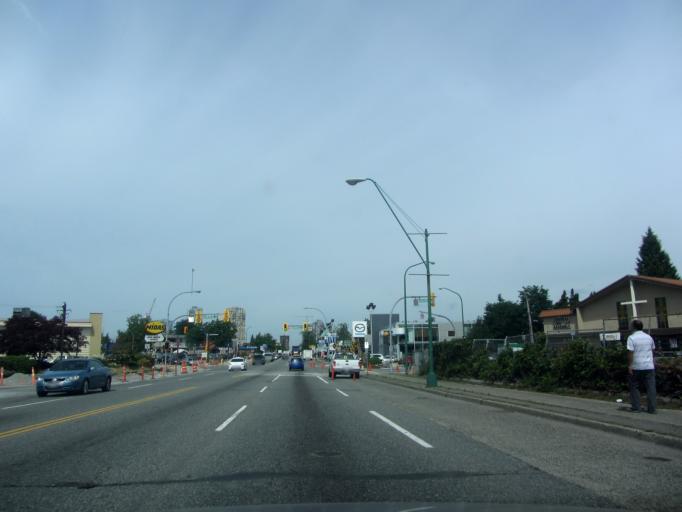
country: CA
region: British Columbia
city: Burnaby
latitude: 49.2184
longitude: -122.9579
